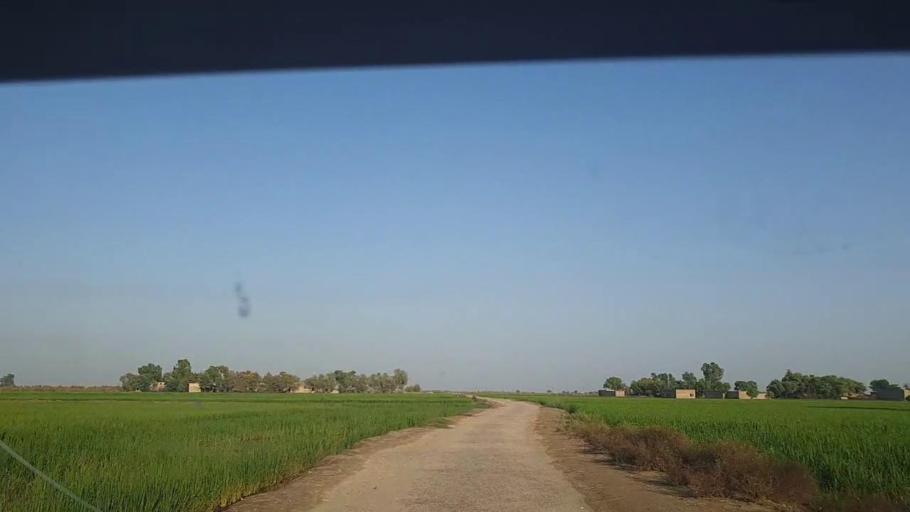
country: PK
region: Sindh
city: Thul
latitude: 28.2123
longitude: 68.8831
